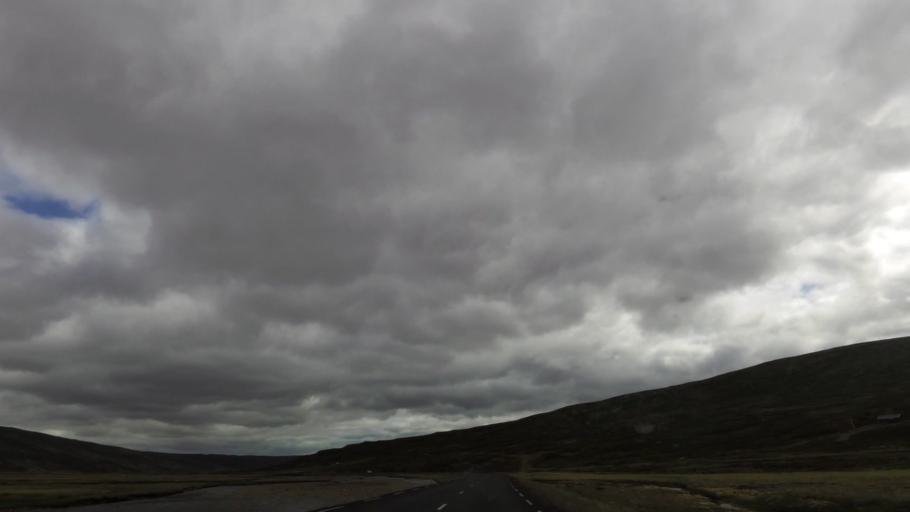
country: IS
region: West
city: Stykkisholmur
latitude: 65.7582
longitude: -21.8699
